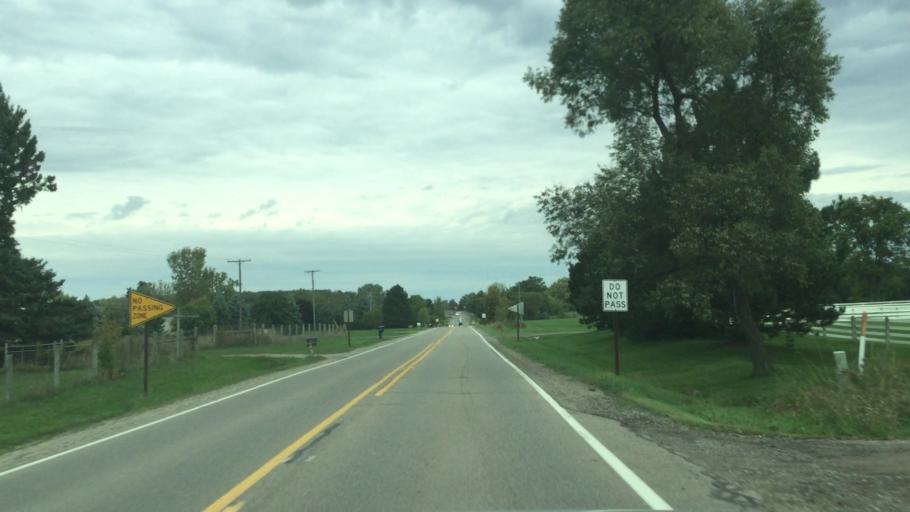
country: US
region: Michigan
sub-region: Livingston County
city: Howell
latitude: 42.6686
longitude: -83.8770
